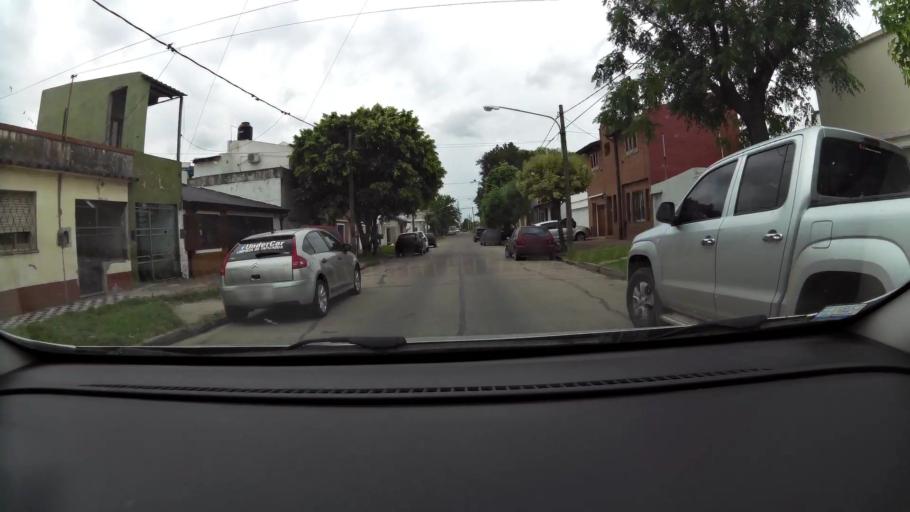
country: AR
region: Buenos Aires
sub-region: Partido de Campana
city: Campana
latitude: -34.1673
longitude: -58.9516
